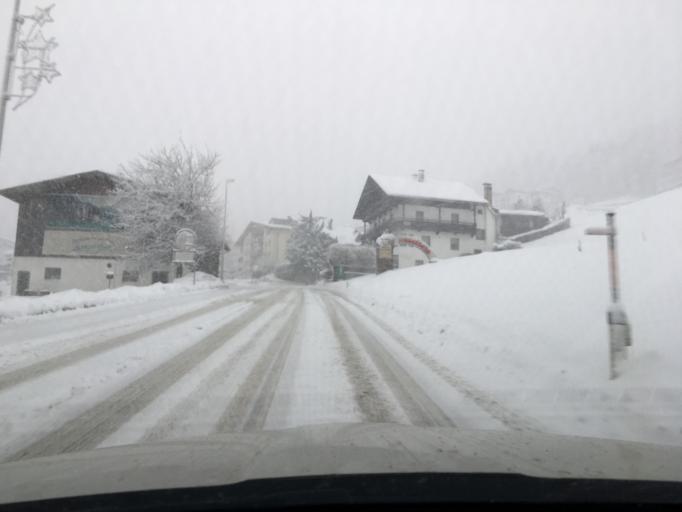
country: AT
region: Tyrol
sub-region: Politischer Bezirk Schwaz
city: Mayrhofen
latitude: 47.1564
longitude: 11.8283
